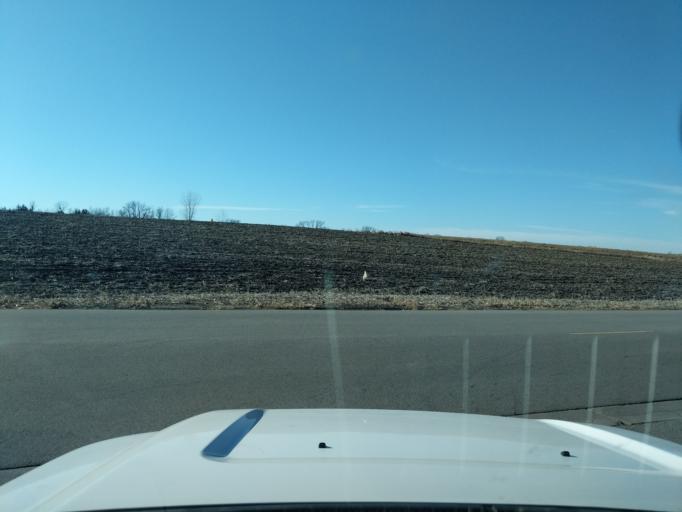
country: US
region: Minnesota
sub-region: Yellow Medicine County
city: Granite Falls
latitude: 44.7631
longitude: -95.5277
